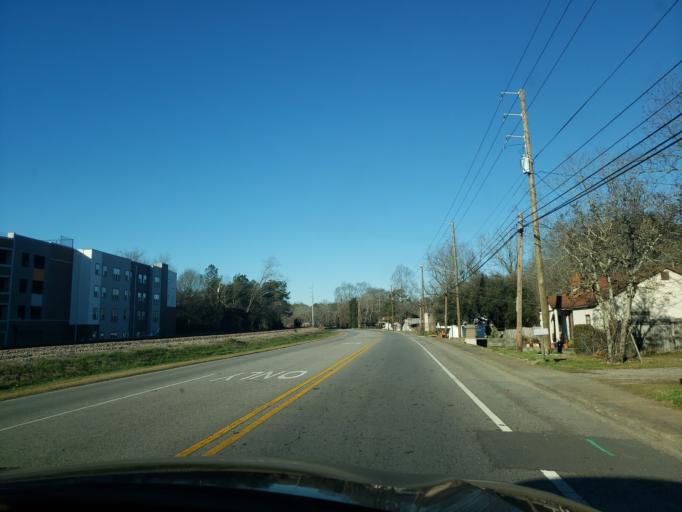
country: US
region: Alabama
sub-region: Lee County
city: Auburn
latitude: 32.6103
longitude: -85.4992
